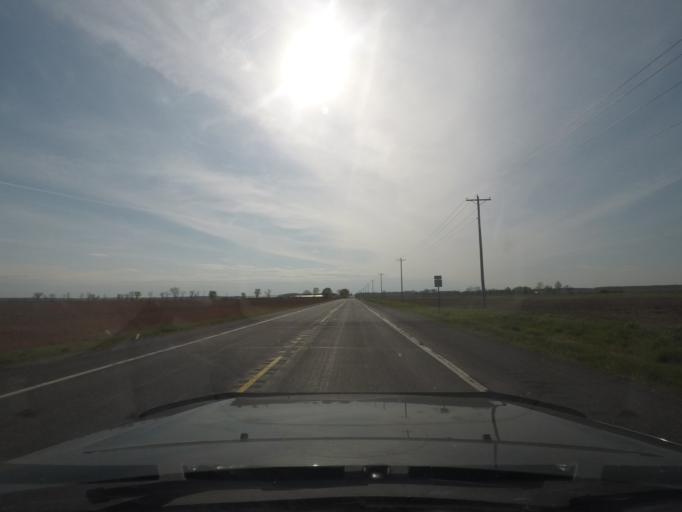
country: US
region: Michigan
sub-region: Berrien County
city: Three Oaks
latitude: 41.7983
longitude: -86.5429
